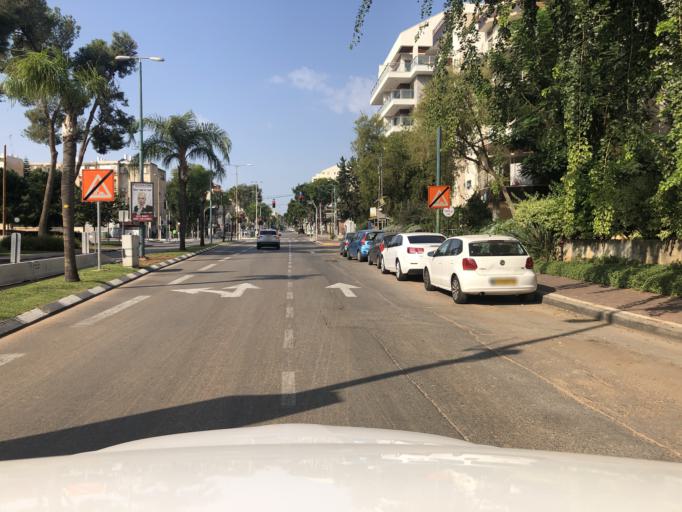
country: IL
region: Central District
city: Kfar Saba
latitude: 32.1735
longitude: 34.9165
